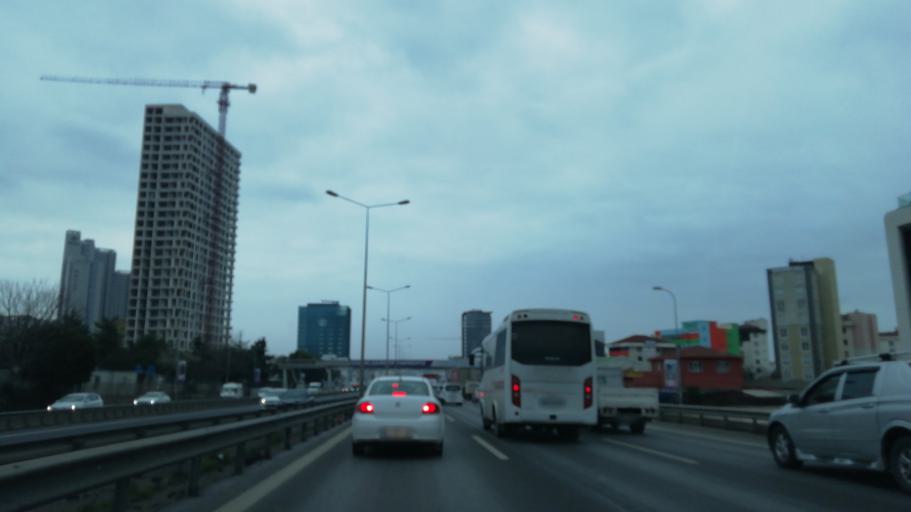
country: TR
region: Istanbul
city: Pendik
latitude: 40.8988
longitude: 29.2225
